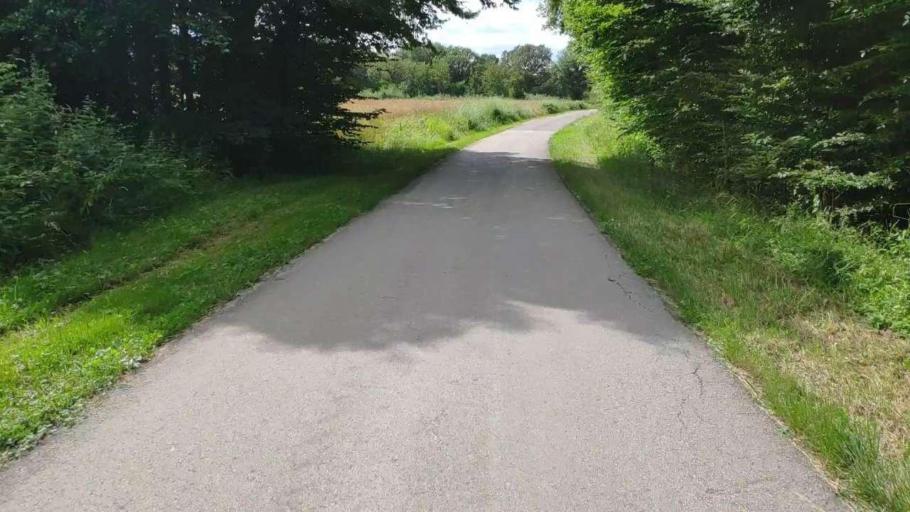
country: FR
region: Franche-Comte
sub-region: Departement du Jura
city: Bletterans
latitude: 46.8073
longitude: 5.4430
